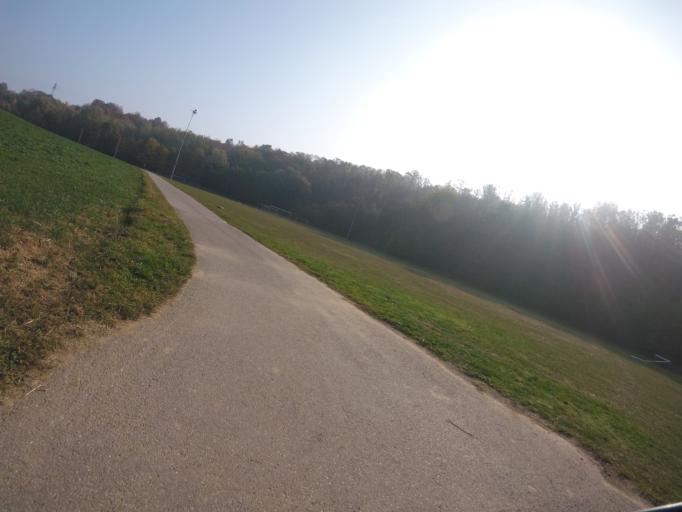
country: DE
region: Baden-Wuerttemberg
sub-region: Regierungsbezirk Stuttgart
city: Mittelschontal
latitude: 48.9384
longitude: 9.4111
